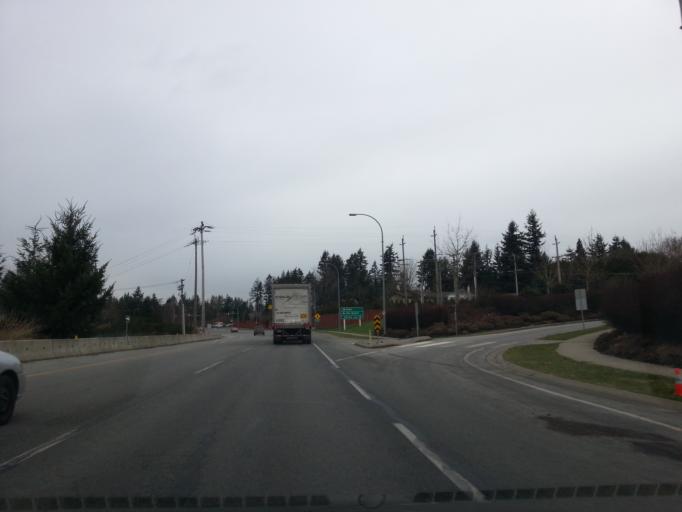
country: CA
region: British Columbia
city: Surrey
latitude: 49.1048
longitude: -122.8284
